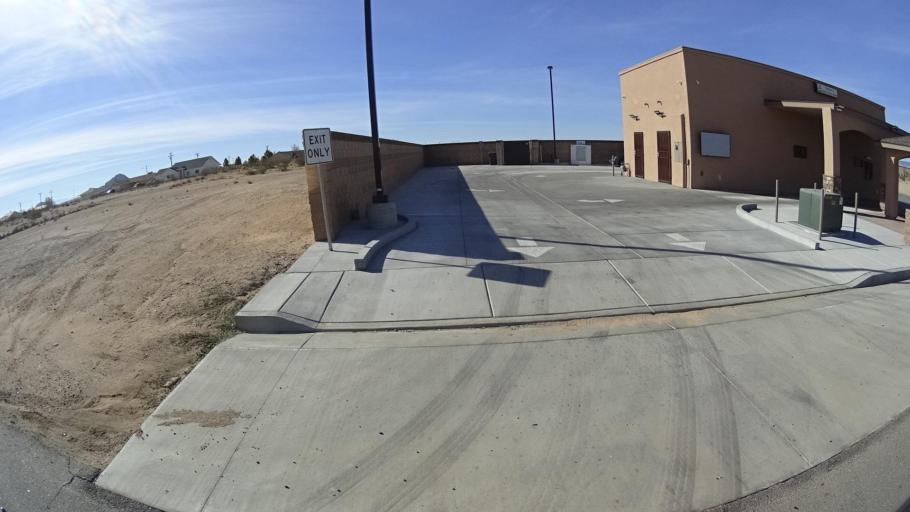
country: US
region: California
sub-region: Kern County
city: California City
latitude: 35.1189
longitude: -117.9386
